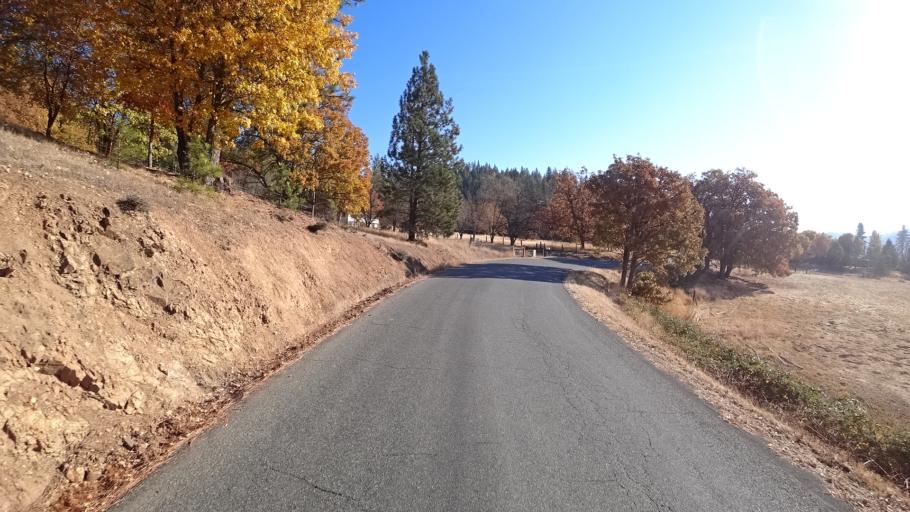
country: US
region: California
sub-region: Siskiyou County
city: Yreka
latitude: 41.6385
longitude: -122.9847
